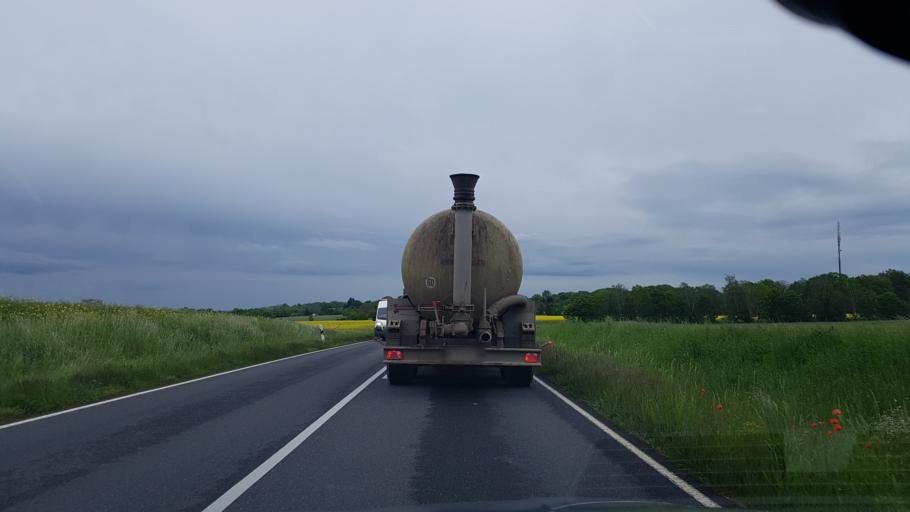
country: DE
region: Brandenburg
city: Drahnsdorf
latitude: 51.8177
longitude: 13.5884
